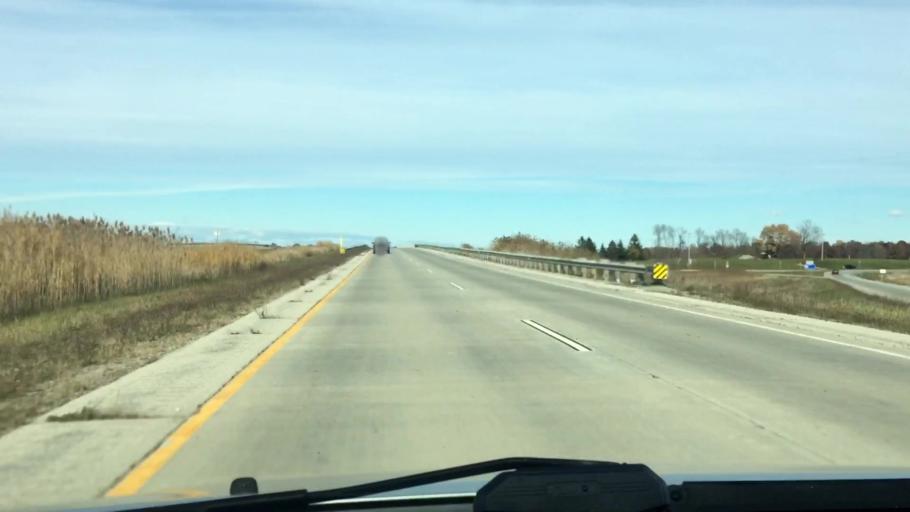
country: US
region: Wisconsin
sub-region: Brown County
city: Bellevue
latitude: 44.5362
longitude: -87.8813
